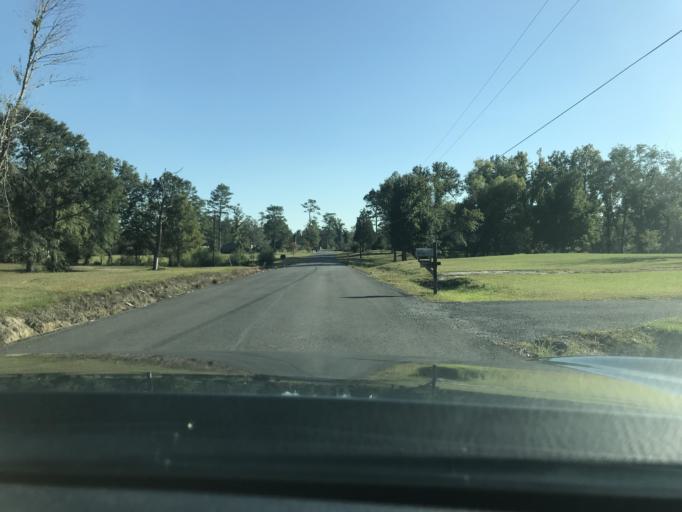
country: US
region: Louisiana
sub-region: Calcasieu Parish
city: Westlake
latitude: 30.3217
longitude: -93.2729
